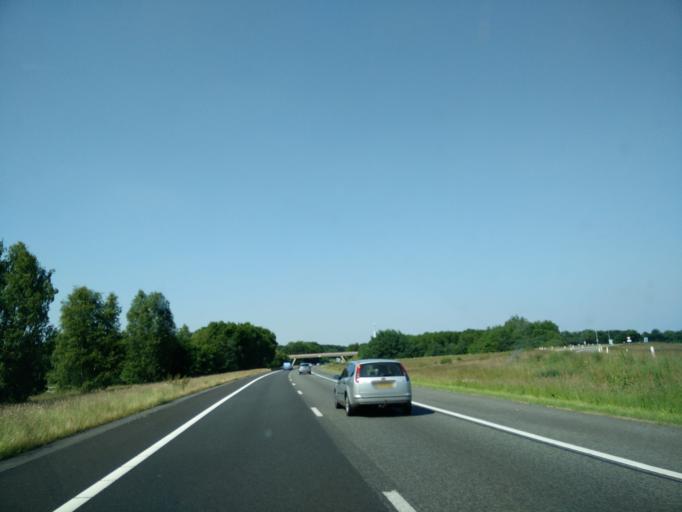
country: NL
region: Drenthe
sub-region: Gemeente Hoogeveen
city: Hoogeveen
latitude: 52.8122
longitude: 6.4607
